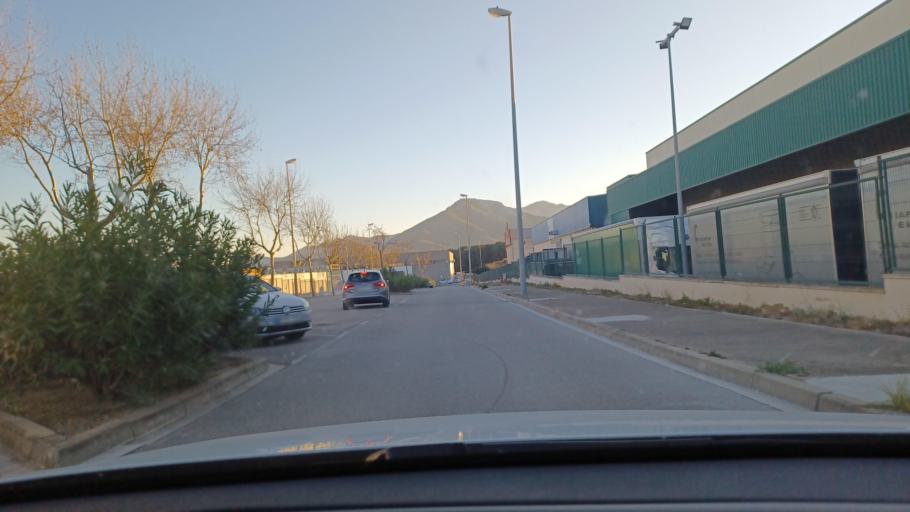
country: ES
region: Catalonia
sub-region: Provincia de Tarragona
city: Amposta
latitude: 40.7040
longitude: 0.5604
